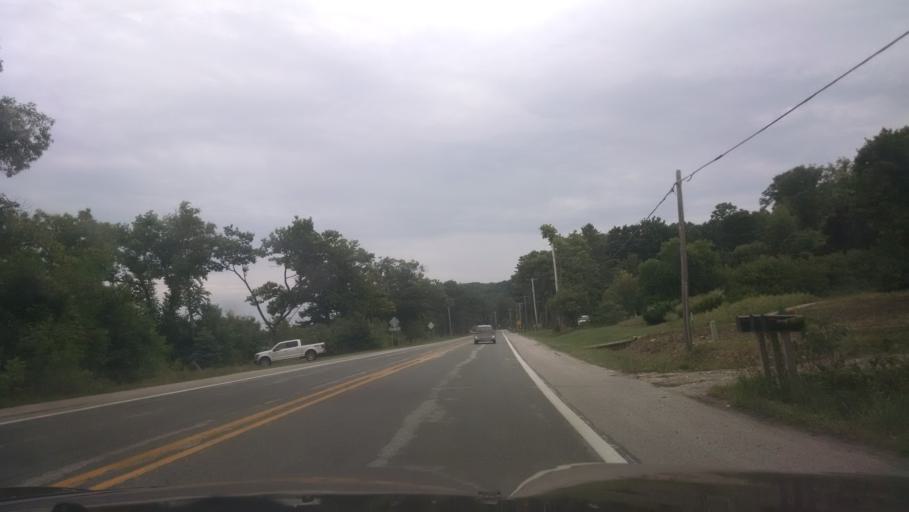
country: US
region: Michigan
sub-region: Leelanau County
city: Greilickville
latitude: 44.8361
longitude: -85.6514
